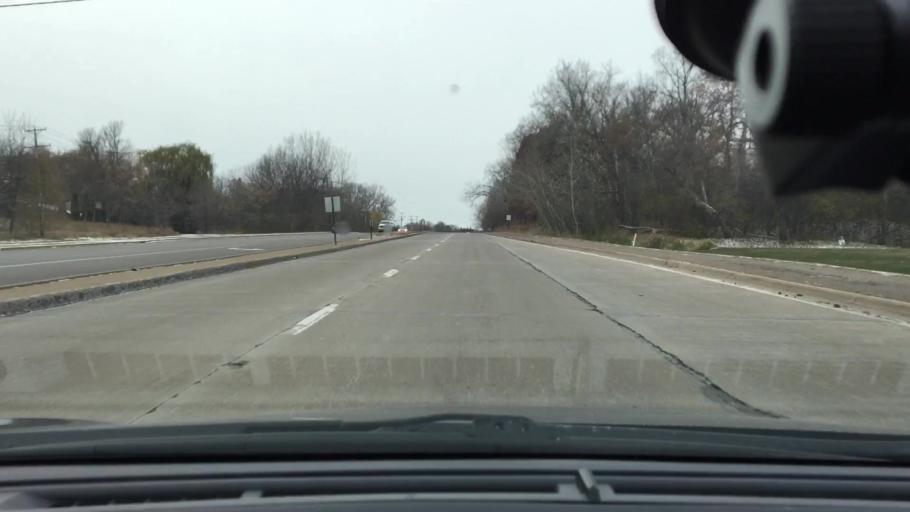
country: US
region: Minnesota
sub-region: Hennepin County
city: New Hope
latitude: 45.0333
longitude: -93.4098
